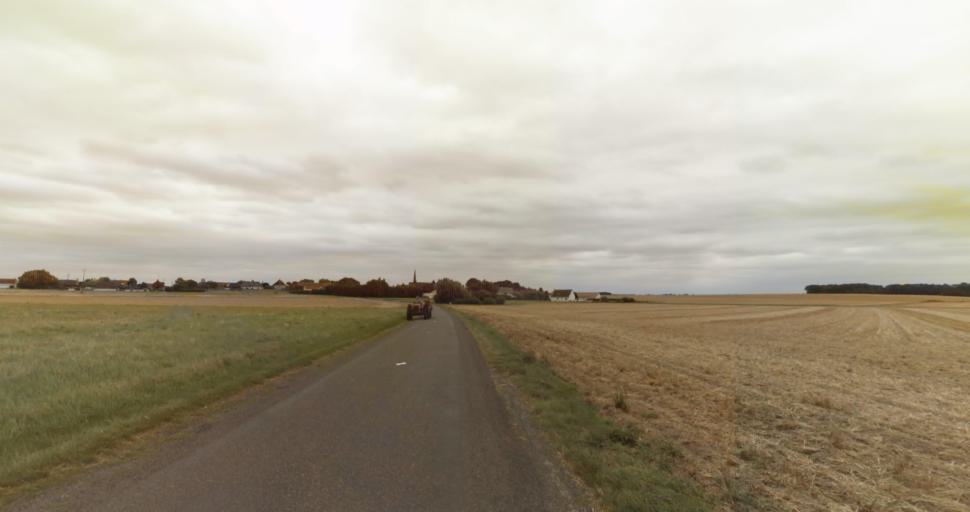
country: FR
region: Haute-Normandie
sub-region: Departement de l'Eure
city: Marcilly-sur-Eure
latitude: 48.9342
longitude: 1.2691
